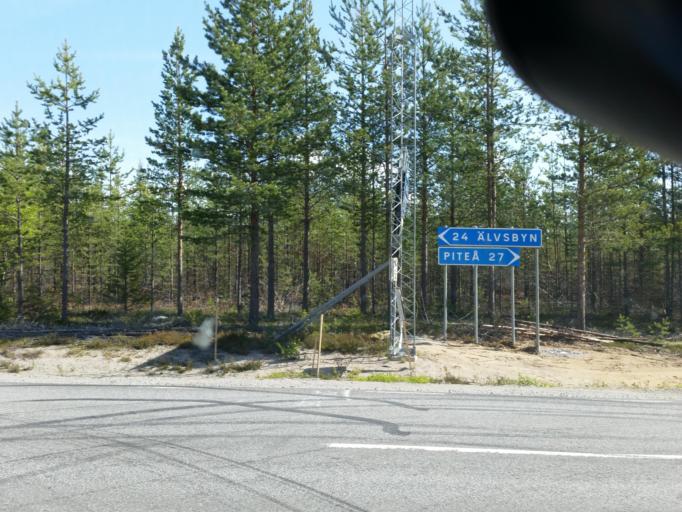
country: SE
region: Norrbotten
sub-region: Pitea Kommun
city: Roknas
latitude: 65.5041
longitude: 21.1945
